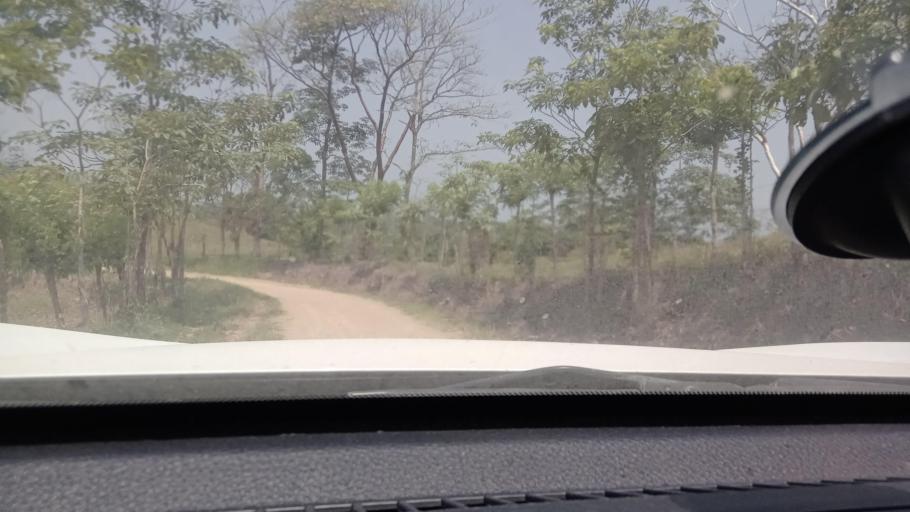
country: MX
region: Tabasco
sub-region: Huimanguillo
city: Francisco Rueda
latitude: 17.4951
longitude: -93.9298
